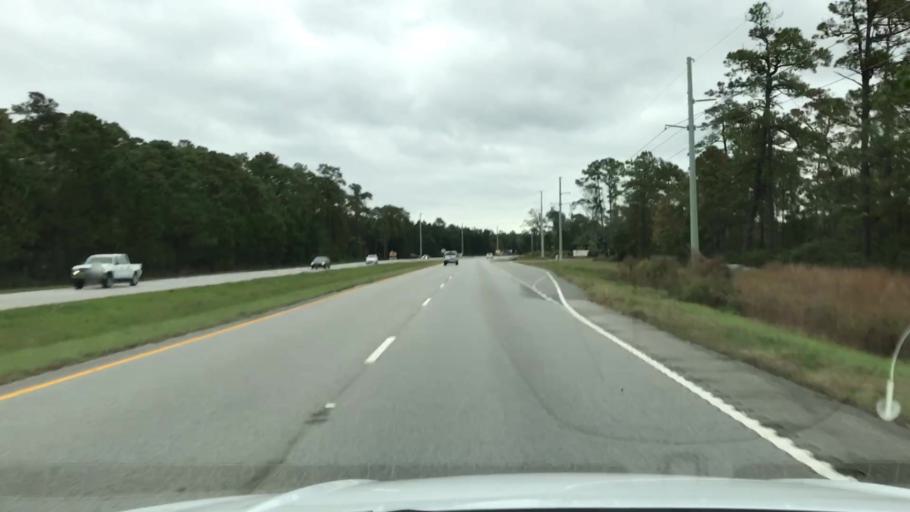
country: US
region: South Carolina
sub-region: Georgetown County
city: Georgetown
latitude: 33.4171
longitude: -79.1818
